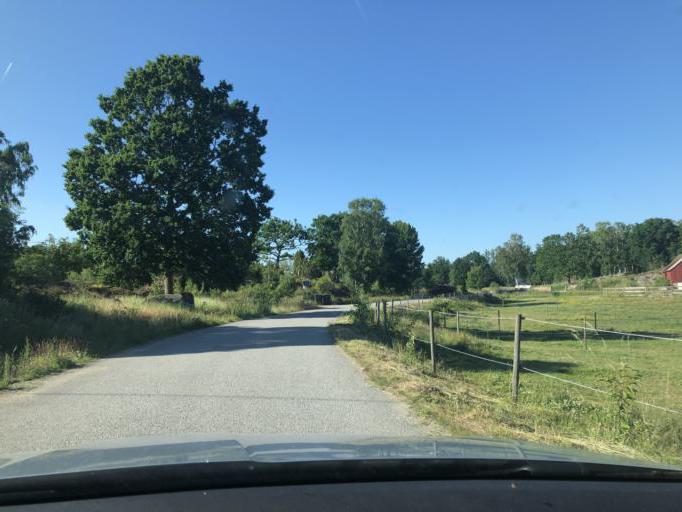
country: SE
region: Blekinge
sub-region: Karlshamns Kommun
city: Morrum
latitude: 56.1588
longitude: 14.7999
